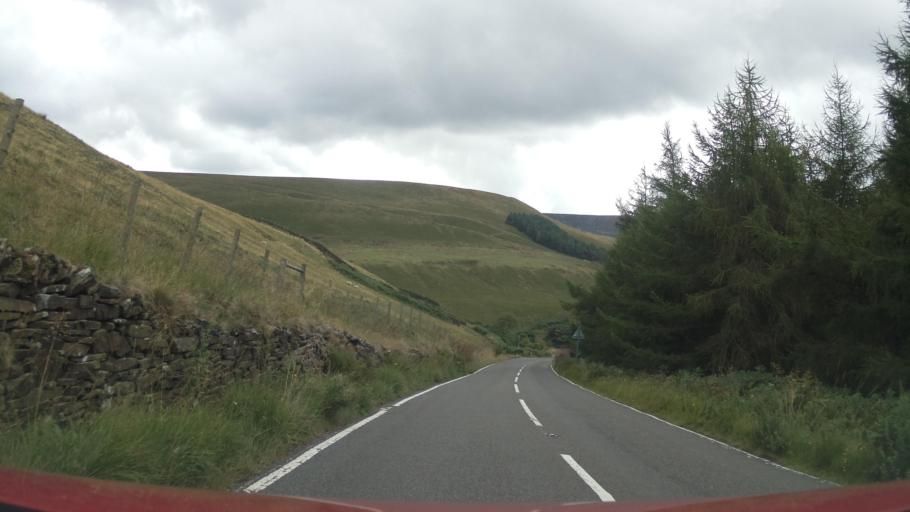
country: GB
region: England
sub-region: Kirklees
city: Meltham
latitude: 53.5059
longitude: -1.8520
